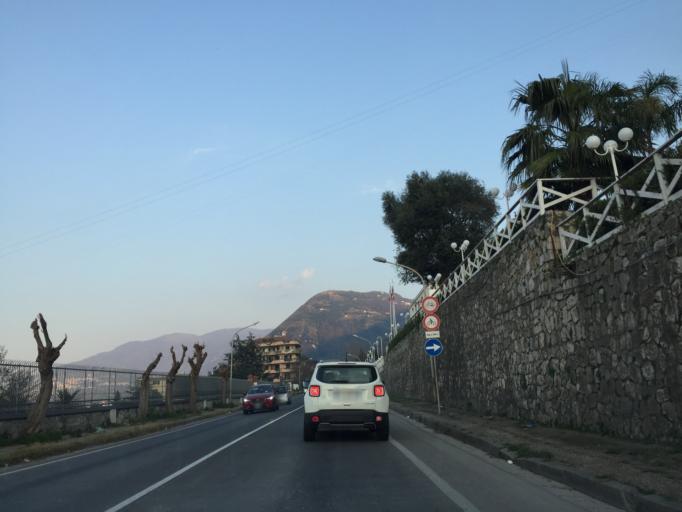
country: IT
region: Campania
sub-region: Provincia di Napoli
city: Castellammare di Stabia
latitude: 40.6879
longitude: 14.4775
